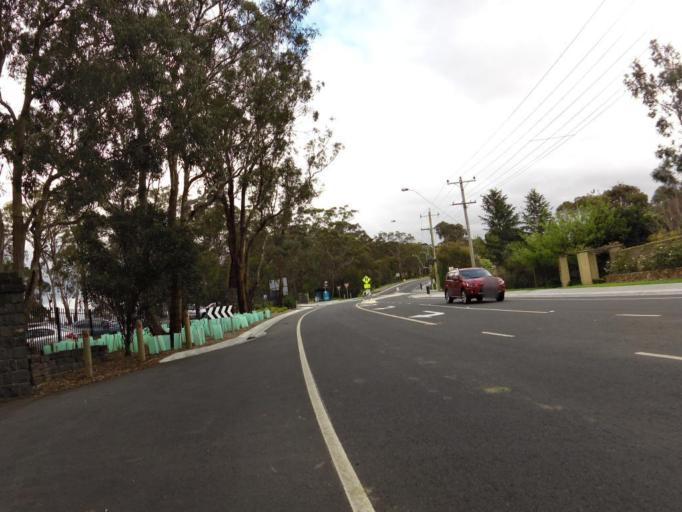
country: AU
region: Victoria
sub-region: Manningham
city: Park Orchards
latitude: -37.7926
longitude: 145.1984
